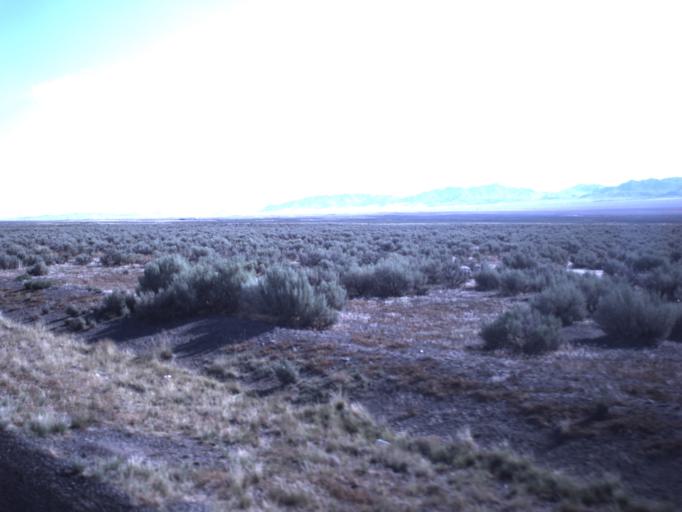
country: US
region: Utah
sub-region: Beaver County
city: Milford
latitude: 38.4267
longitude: -113.0098
